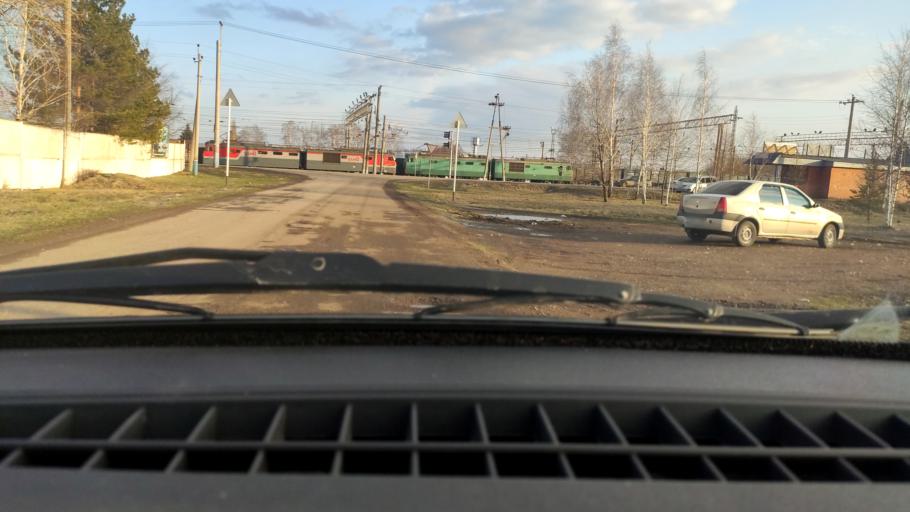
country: RU
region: Bashkortostan
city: Chishmy
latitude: 54.5911
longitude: 55.4030
